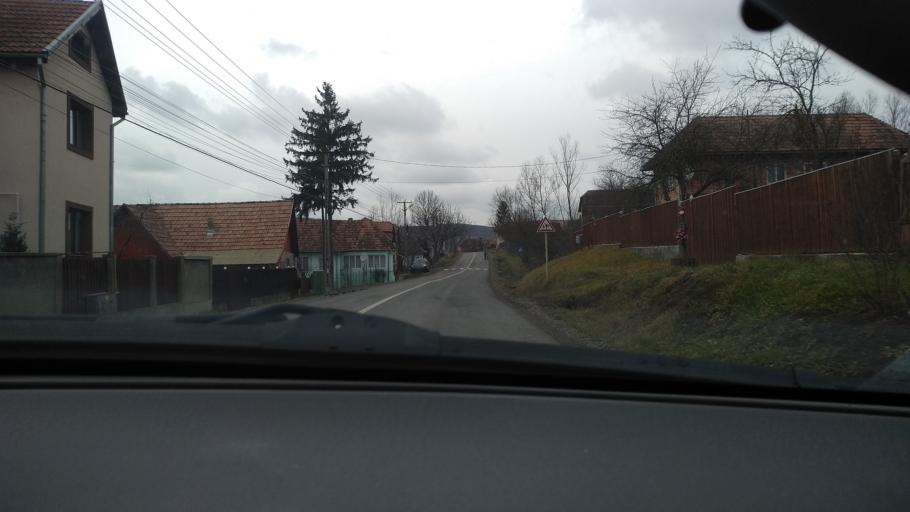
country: RO
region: Mures
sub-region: Comuna Galesti
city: Galesti
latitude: 46.5323
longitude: 24.7666
